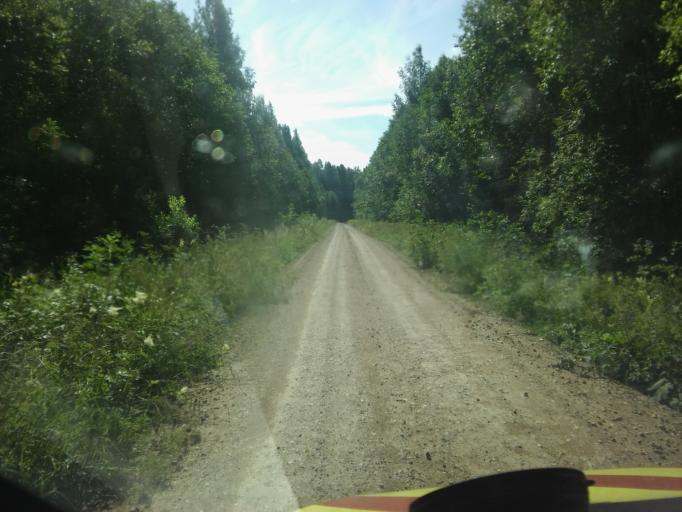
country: EE
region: Paernumaa
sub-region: Paikuse vald
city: Paikuse
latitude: 58.2879
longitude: 24.6999
